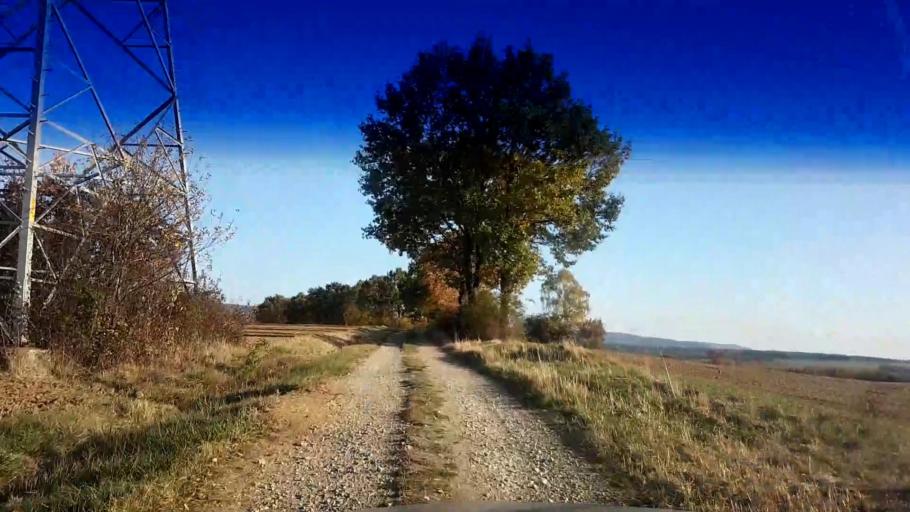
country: DE
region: Bavaria
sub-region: Upper Franconia
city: Memmelsdorf
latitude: 49.9590
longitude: 10.9786
